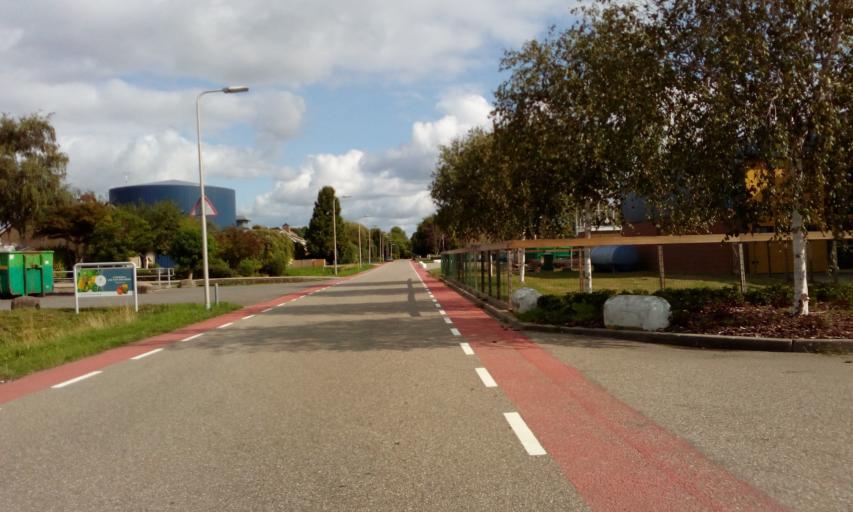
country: NL
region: South Holland
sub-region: Gemeente Lansingerland
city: Bleiswijk
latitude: 51.9978
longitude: 4.5369
